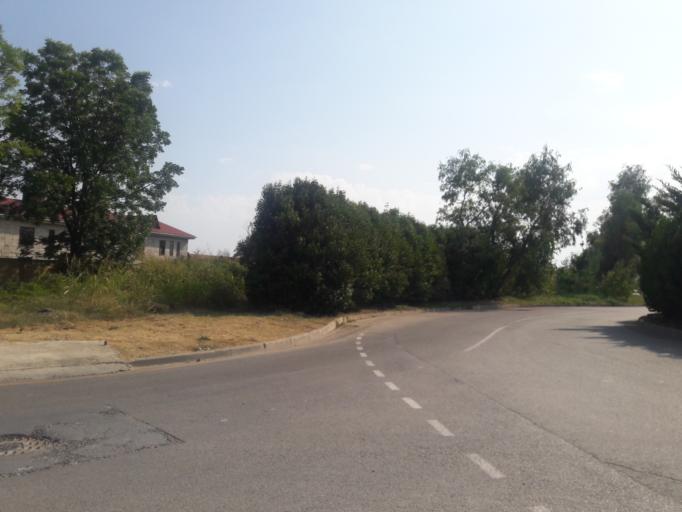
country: RU
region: Krasnodarskiy
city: Vysokoye
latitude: 43.3940
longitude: 40.0025
